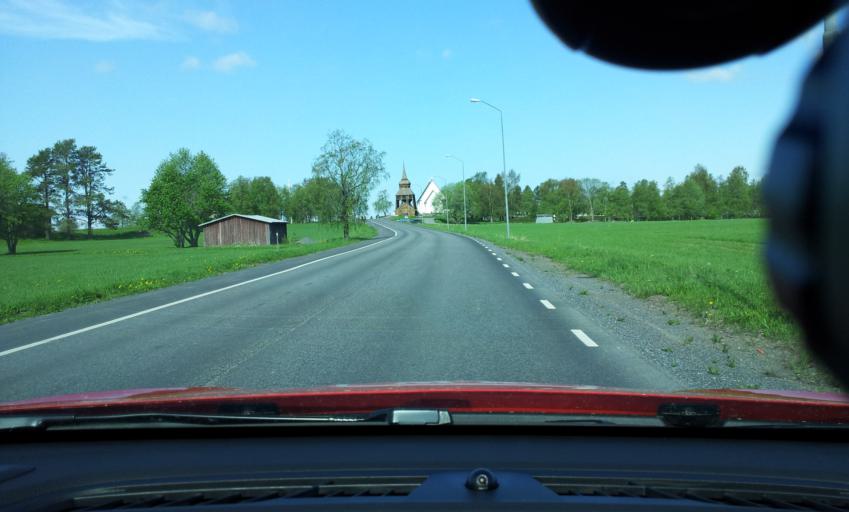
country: SE
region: Jaemtland
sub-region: OEstersunds Kommun
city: Ostersund
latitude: 63.1773
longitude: 14.5263
